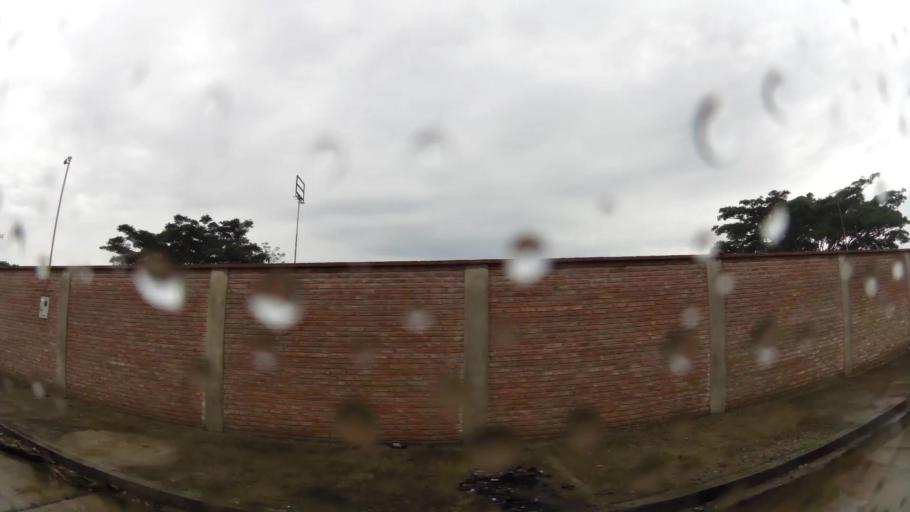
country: BO
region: Santa Cruz
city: Santa Cruz de la Sierra
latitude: -17.8073
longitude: -63.1997
